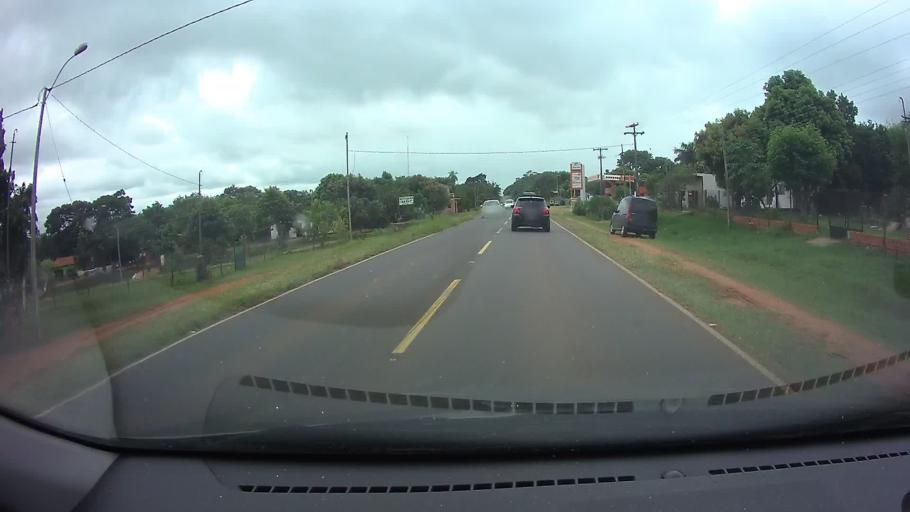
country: PY
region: Paraguari
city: Carapegua
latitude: -25.7418
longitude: -57.2805
